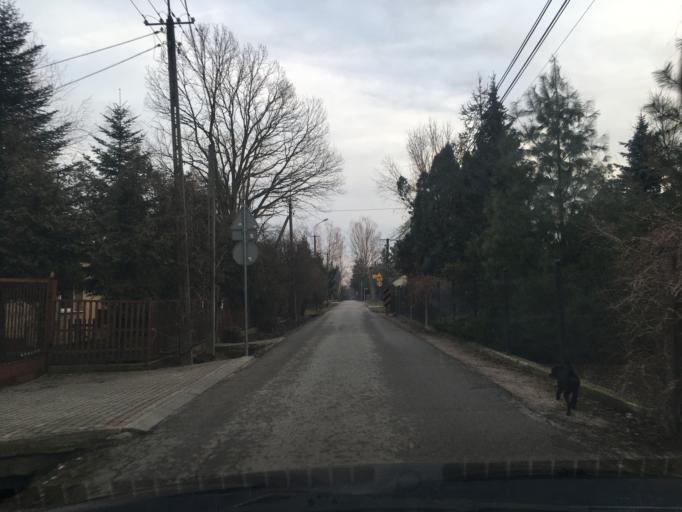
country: PL
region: Masovian Voivodeship
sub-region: Powiat piaseczynski
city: Lesznowola
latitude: 52.0393
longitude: 20.9561
